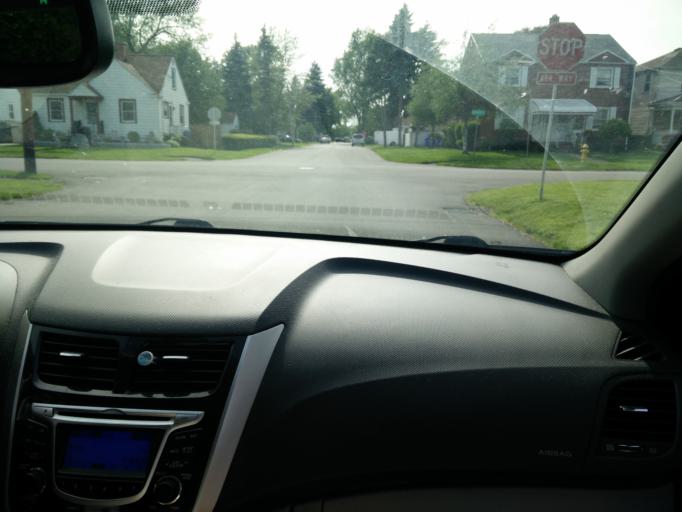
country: US
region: New York
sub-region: Erie County
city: West Seneca
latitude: 42.8364
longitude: -78.7983
